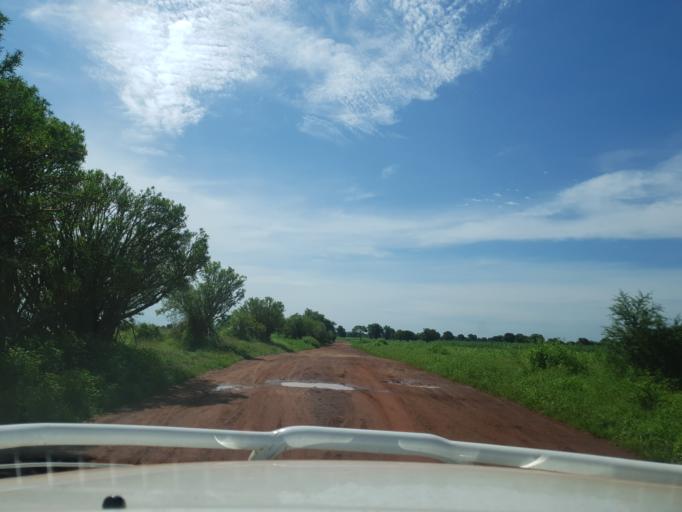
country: ML
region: Koulikoro
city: Banamba
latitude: 13.2782
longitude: -7.5489
